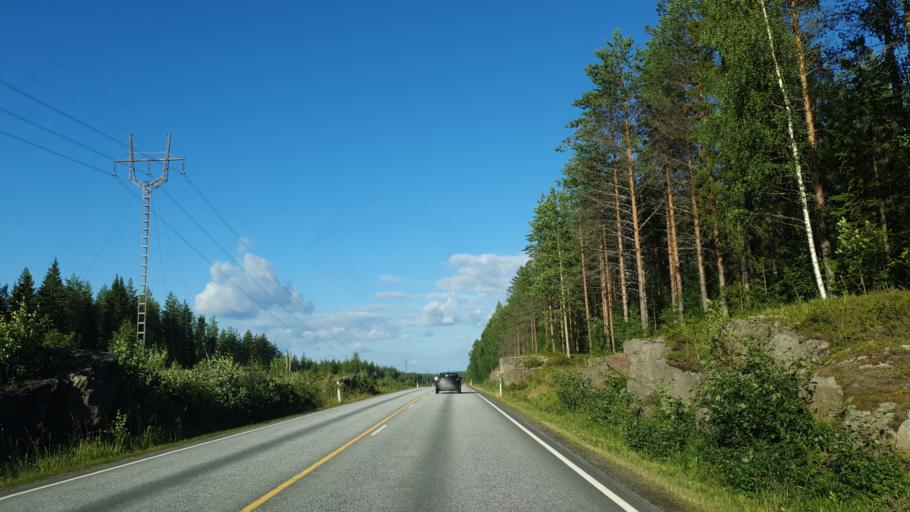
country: FI
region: North Karelia
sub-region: Joensuu
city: Outokumpu
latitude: 62.5276
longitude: 29.0723
